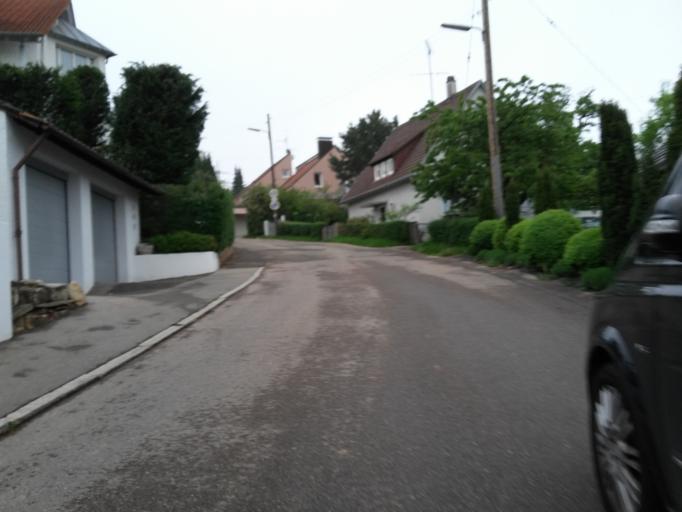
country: DE
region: Baden-Wuerttemberg
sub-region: Regierungsbezirk Stuttgart
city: Esslingen
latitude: 48.7463
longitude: 9.3460
